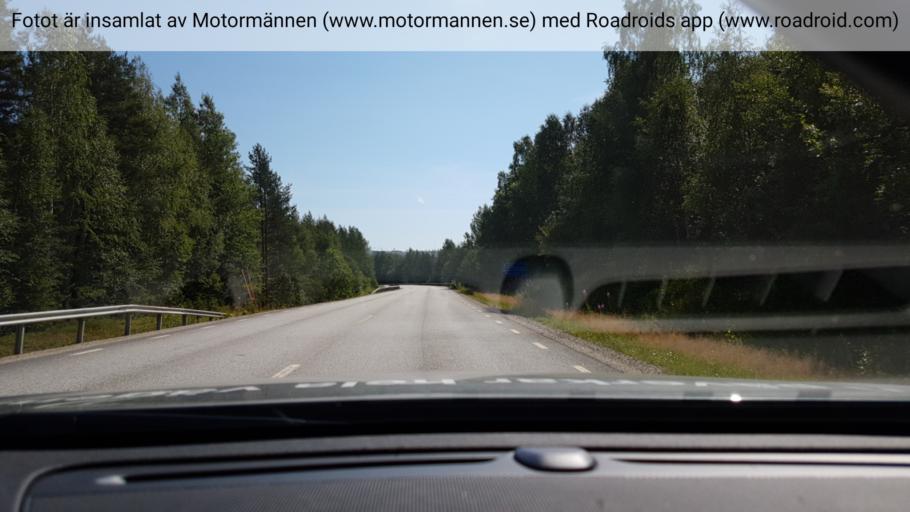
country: SE
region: Vaesterbotten
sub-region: Vindelns Kommun
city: Vindeln
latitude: 64.3150
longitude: 19.5861
